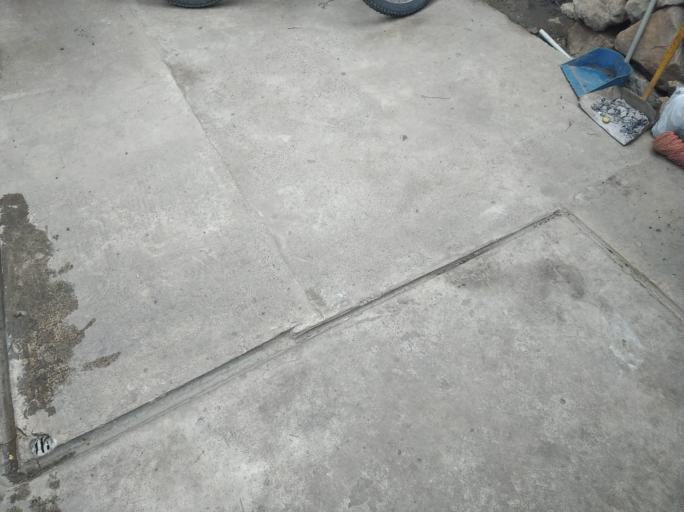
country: PE
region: Lima
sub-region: Oyon
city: Oyon
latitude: -10.6681
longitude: -76.7745
